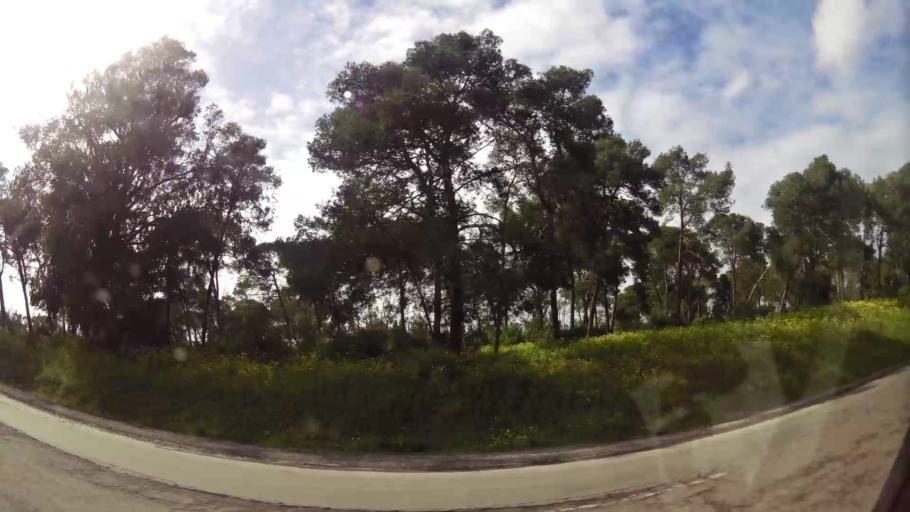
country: MA
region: Grand Casablanca
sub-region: Mohammedia
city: Mohammedia
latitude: 33.6538
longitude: -7.4018
